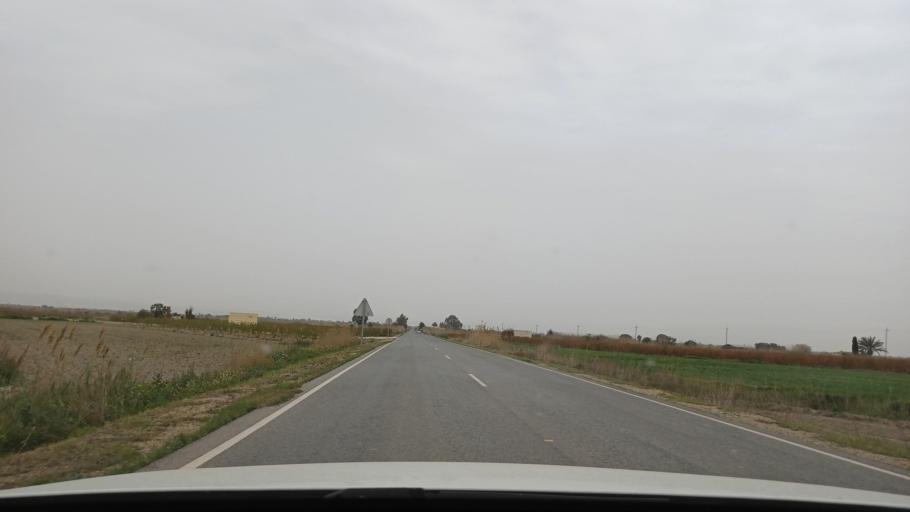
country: ES
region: Valencia
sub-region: Provincia de Alicante
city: Daya Vieja
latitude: 38.1606
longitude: -0.7032
